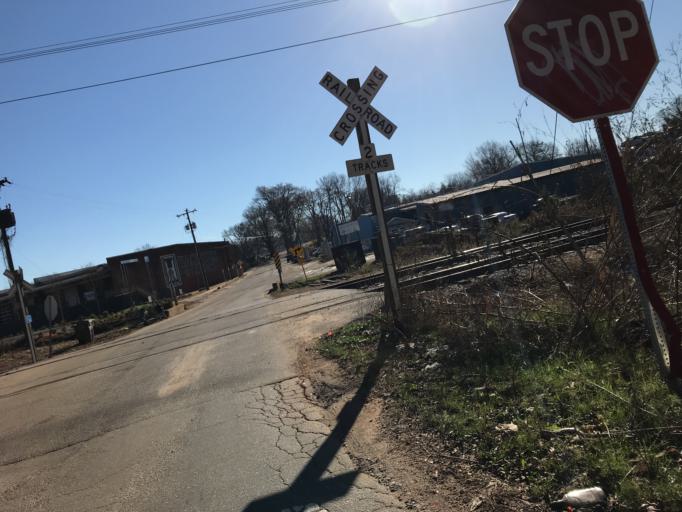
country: US
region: South Carolina
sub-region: Greenville County
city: Sans Souci
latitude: 34.8665
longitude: -82.4176
